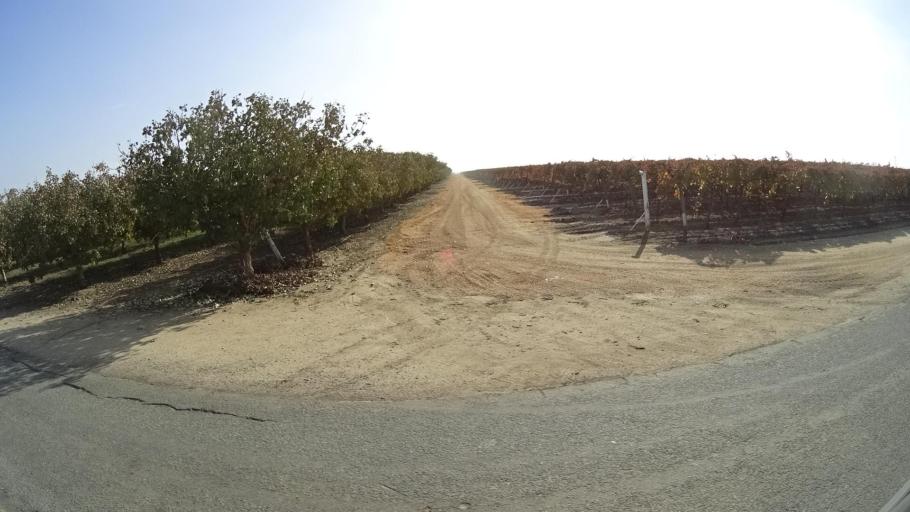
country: US
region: California
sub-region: Tulare County
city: Richgrove
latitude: 35.7908
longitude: -119.0784
